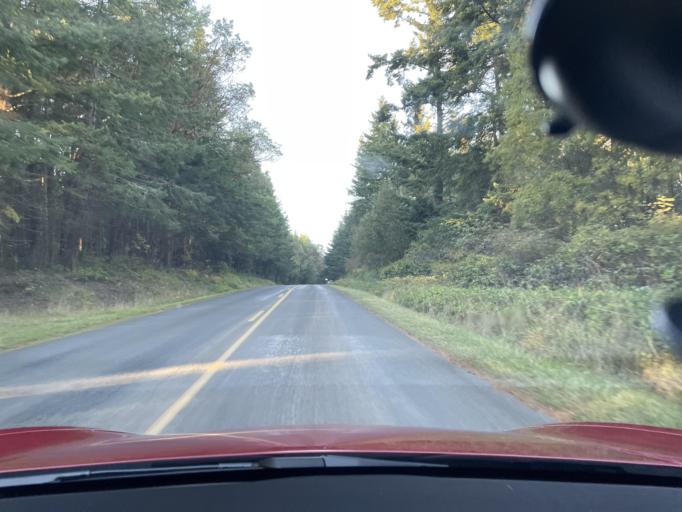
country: US
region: Washington
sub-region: San Juan County
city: Friday Harbor
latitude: 48.5552
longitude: -123.1646
